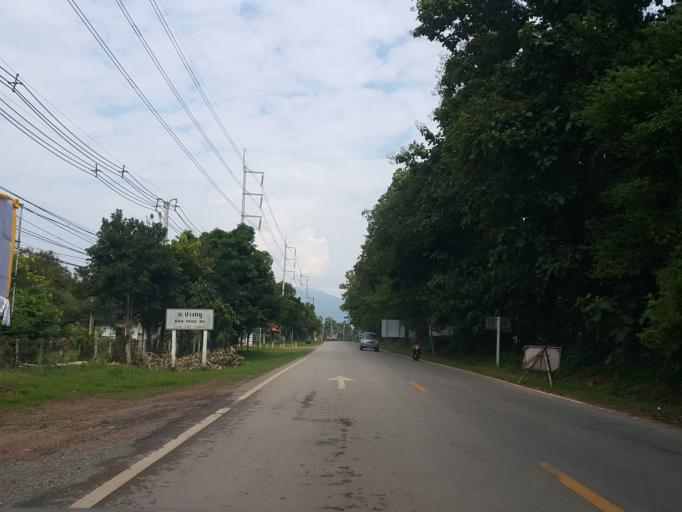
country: TH
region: Mae Hong Son
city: Mae Hong Son
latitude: 19.3441
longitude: 97.9635
